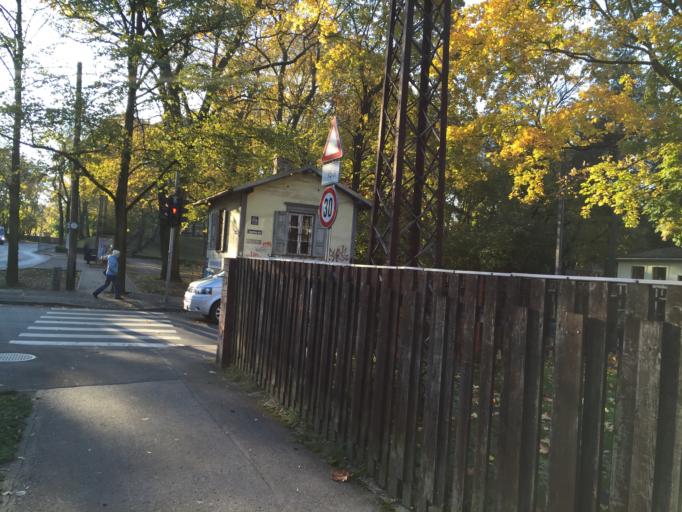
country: LV
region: Riga
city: Riga
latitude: 56.9412
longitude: 24.0693
